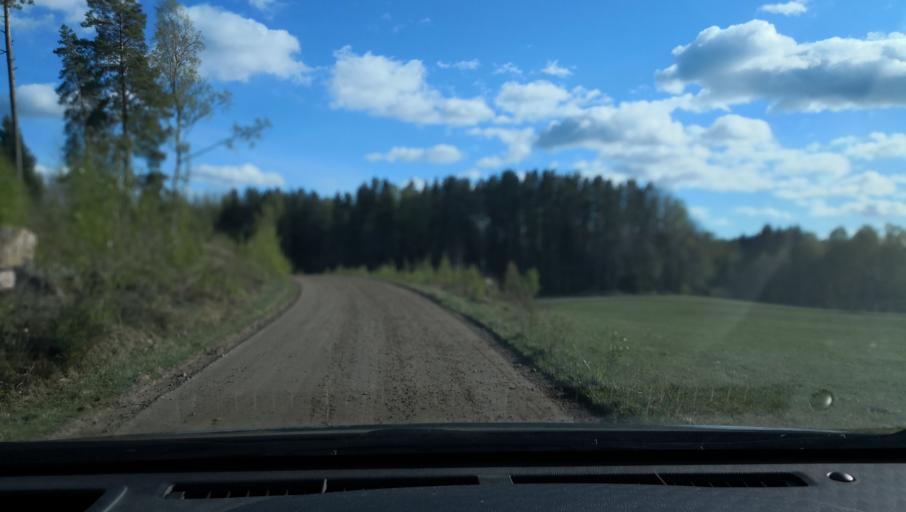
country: SE
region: OErebro
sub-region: Askersunds Kommun
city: Asbro
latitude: 58.8950
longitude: 15.1082
